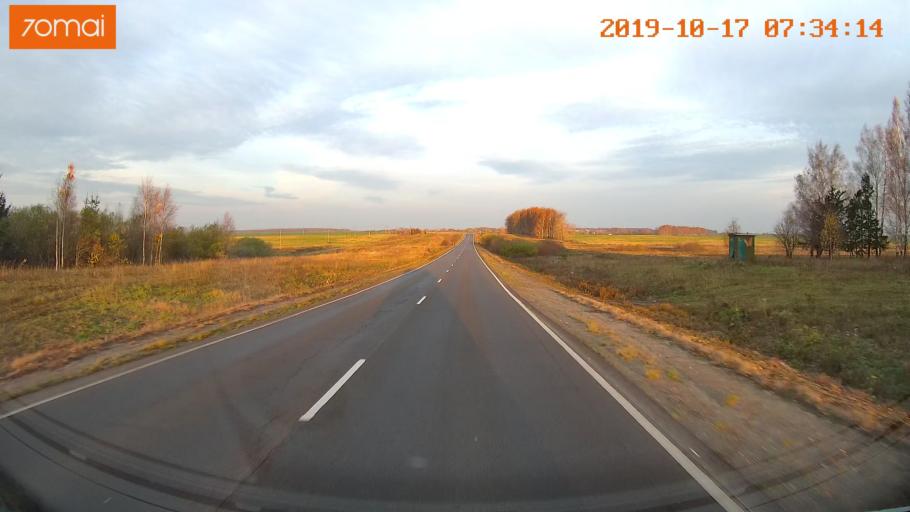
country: RU
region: Ivanovo
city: Gavrilov Posad
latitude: 56.4155
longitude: 39.9460
